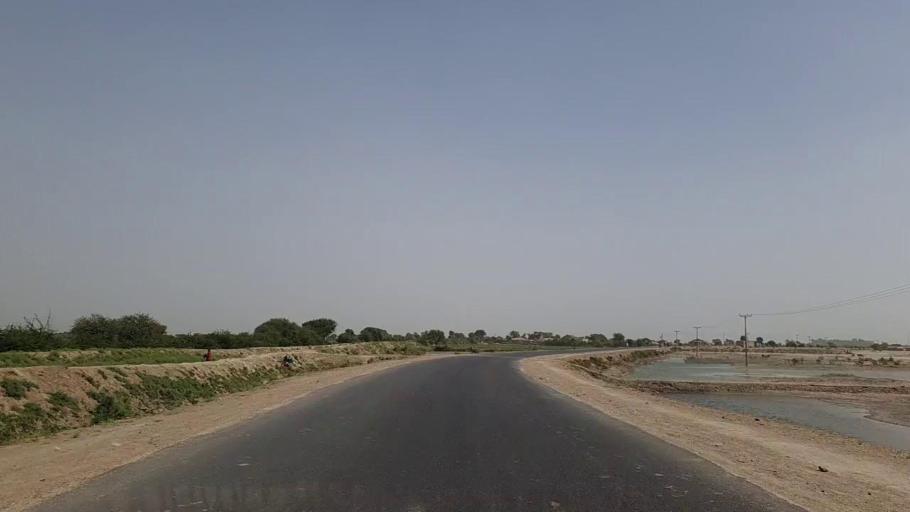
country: PK
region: Sindh
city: Talhar
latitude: 24.8463
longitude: 68.8817
